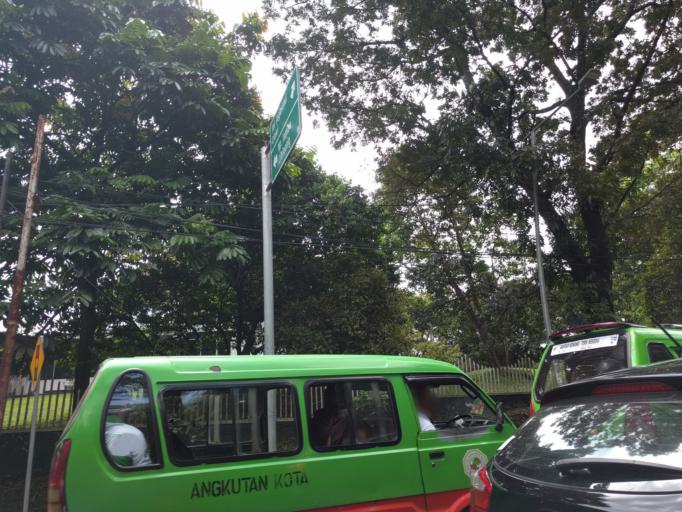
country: ID
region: West Java
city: Bogor
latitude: -6.5948
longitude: 106.8037
